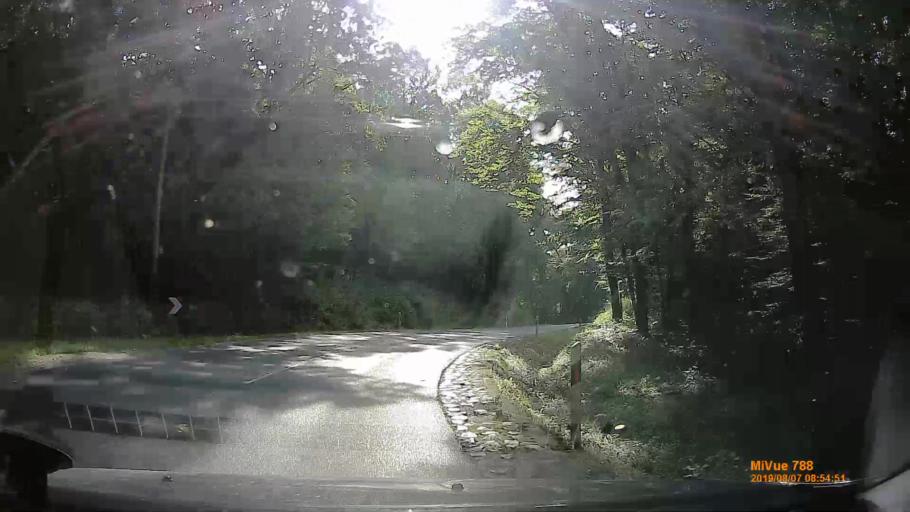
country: HU
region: Zala
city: Zalaegerszeg
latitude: 46.7339
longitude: 16.8707
